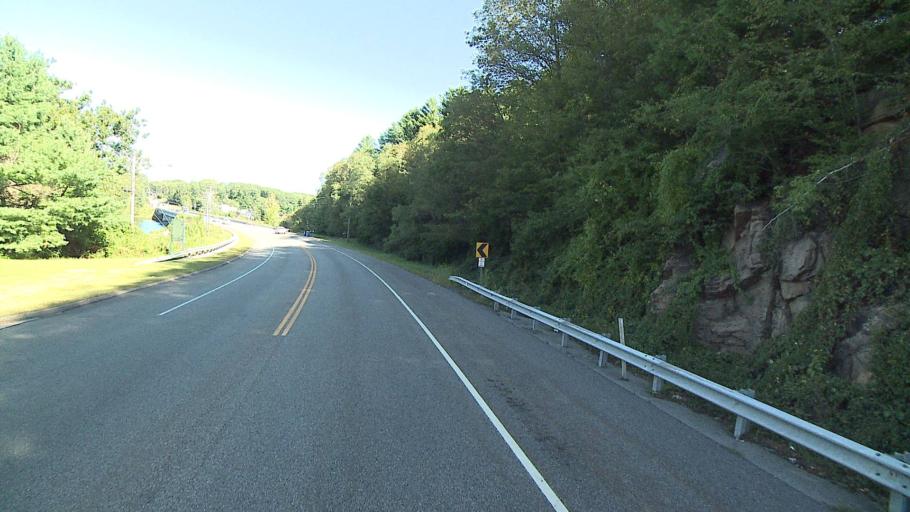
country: US
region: Connecticut
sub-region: New London County
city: Gales Ferry
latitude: 41.4696
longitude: -72.0586
